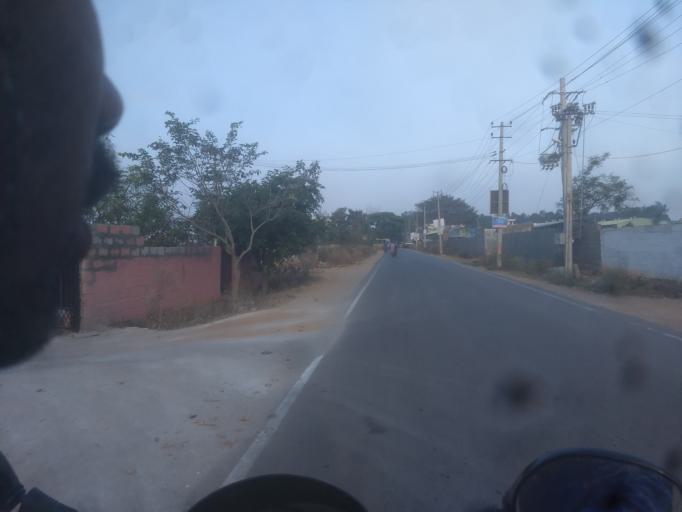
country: IN
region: Karnataka
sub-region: Bangalore Urban
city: Anekal
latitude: 12.8389
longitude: 77.6994
